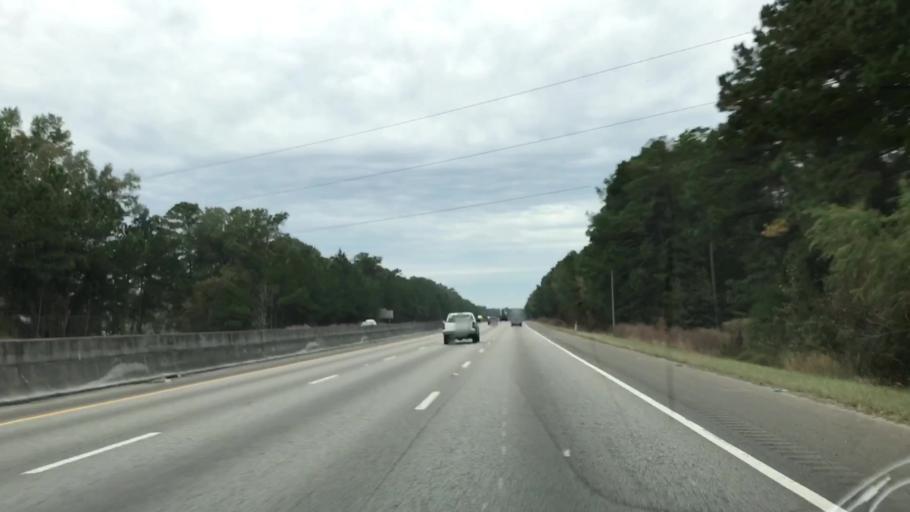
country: US
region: South Carolina
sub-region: Berkeley County
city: Goose Creek
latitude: 32.9513
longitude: -80.0611
